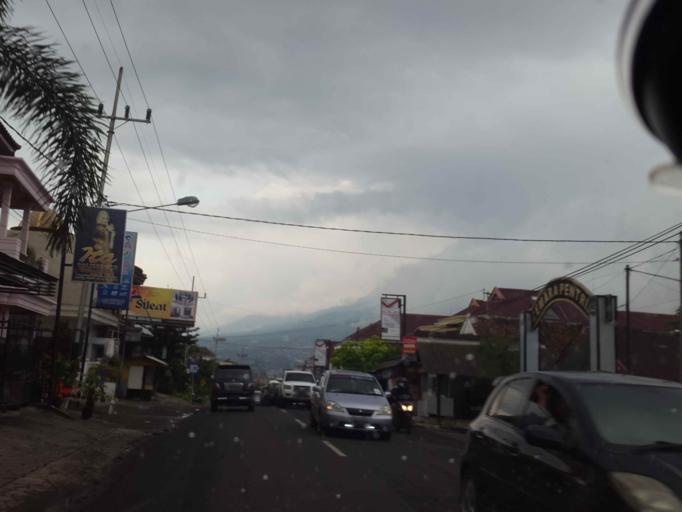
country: ID
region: East Java
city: Batu
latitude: -7.8492
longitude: 112.5280
